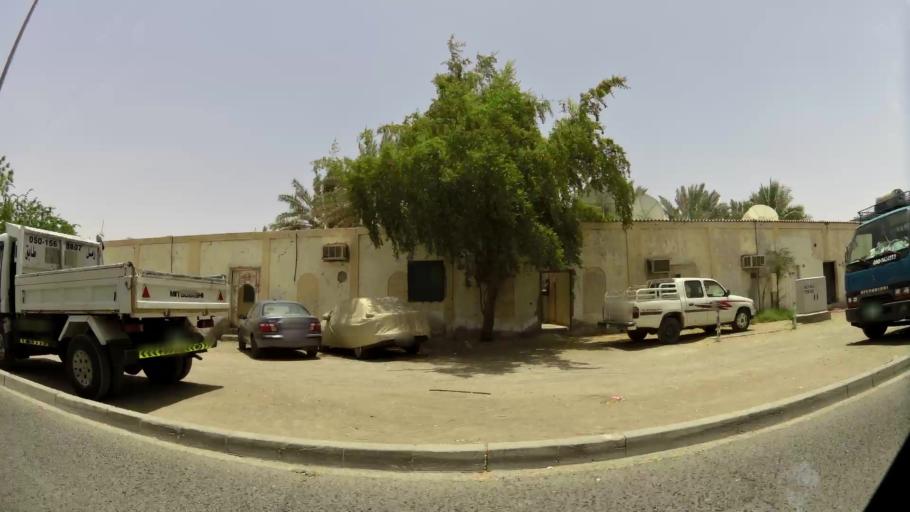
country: AE
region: Abu Dhabi
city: Al Ain
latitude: 24.2067
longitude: 55.7550
